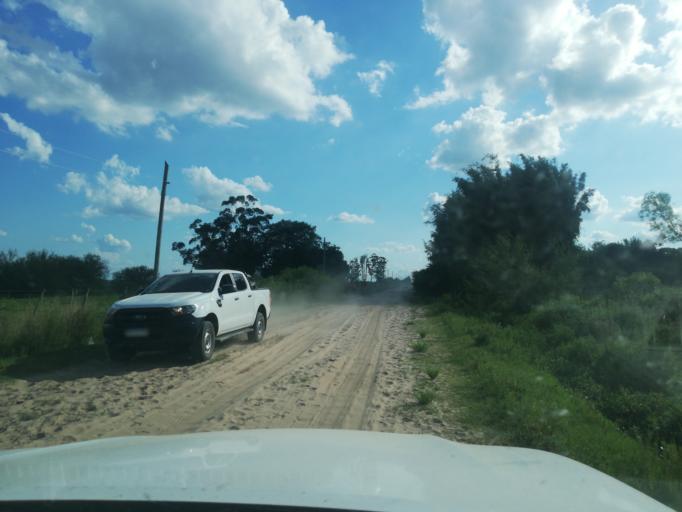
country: AR
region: Corrientes
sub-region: Departamento de San Miguel
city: San Miguel
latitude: -27.9942
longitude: -57.5774
